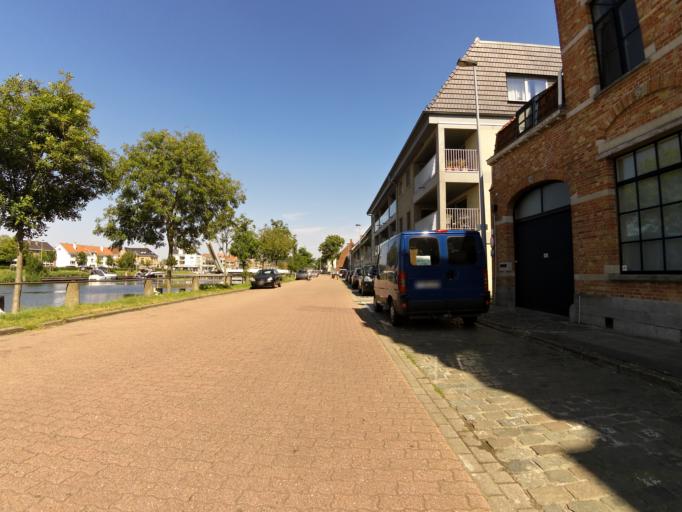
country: BE
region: Flanders
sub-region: Provincie West-Vlaanderen
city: Brugge
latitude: 51.2179
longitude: 3.2073
